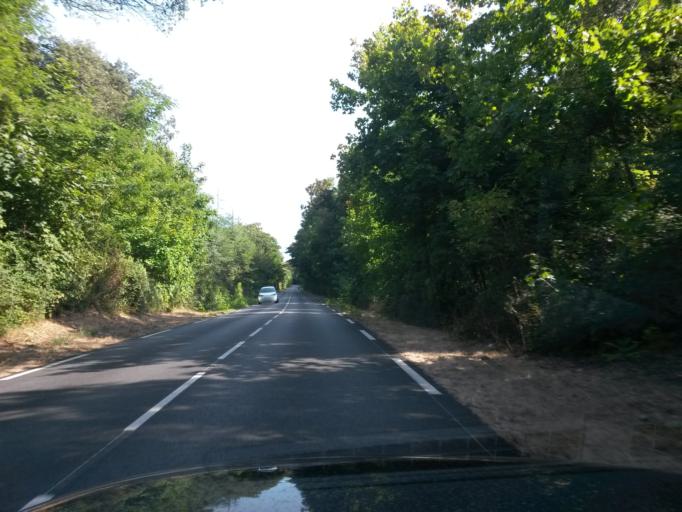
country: FR
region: Pays de la Loire
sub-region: Departement de la Vendee
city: Olonne-sur-Mer
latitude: 46.5663
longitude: -1.8184
